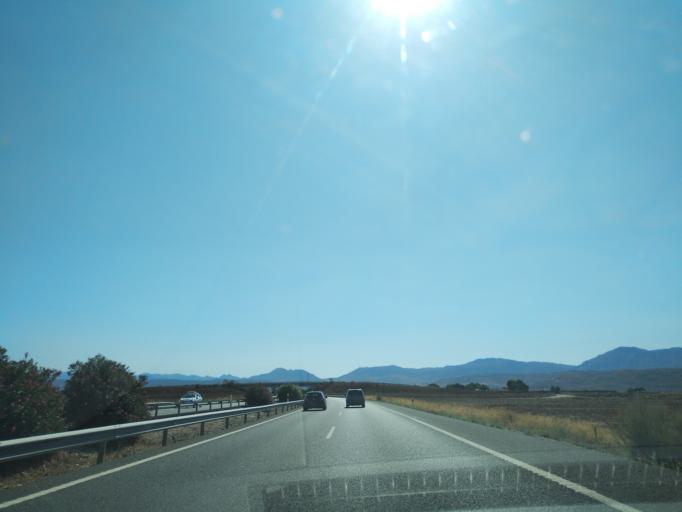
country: ES
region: Andalusia
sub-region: Provincia de Malaga
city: Mollina
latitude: 37.0856
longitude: -4.6215
